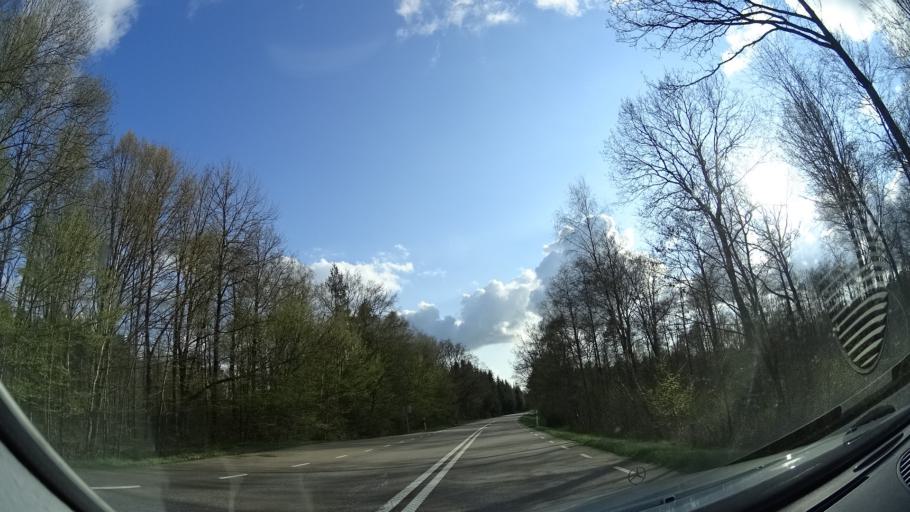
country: SE
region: Skane
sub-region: Klippans Kommun
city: Ljungbyhed
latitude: 56.1195
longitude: 13.2971
